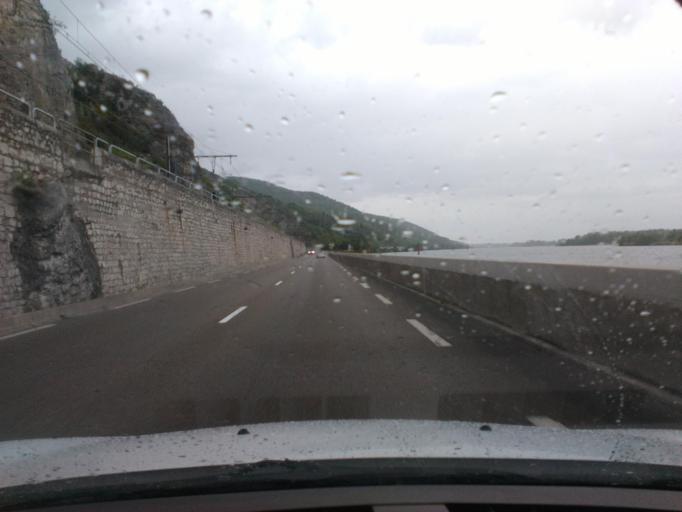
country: FR
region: Rhone-Alpes
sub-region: Departement de l'Ardeche
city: Le Pouzin
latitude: 44.7642
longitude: 4.7526
